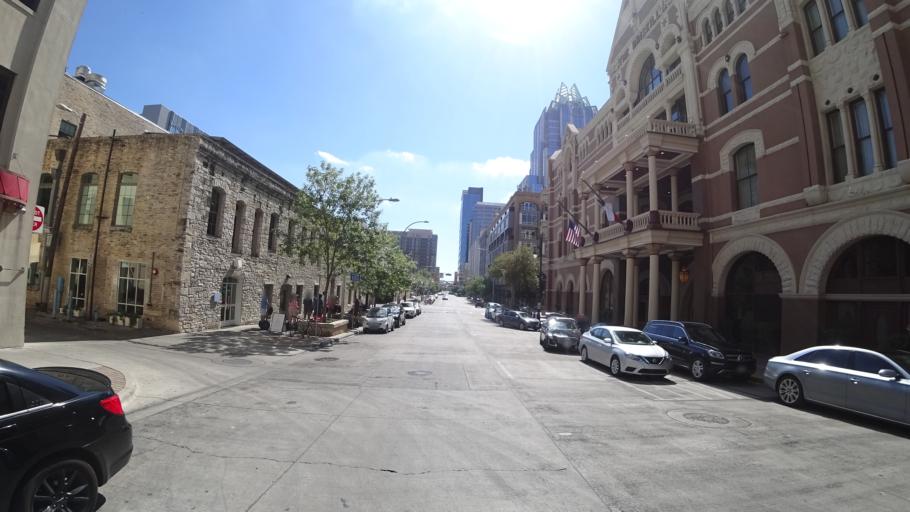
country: US
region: Texas
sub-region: Travis County
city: Austin
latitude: 30.2682
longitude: -97.7412
